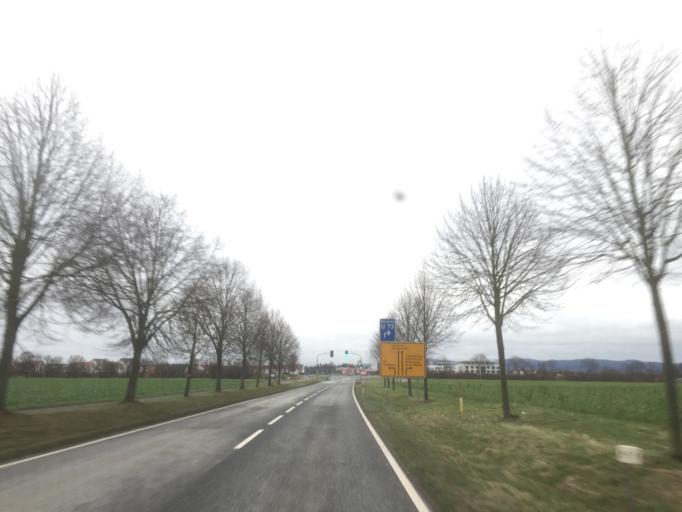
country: DE
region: Hesse
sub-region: Regierungsbezirk Darmstadt
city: Seligenstadt
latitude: 50.0346
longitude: 8.9502
